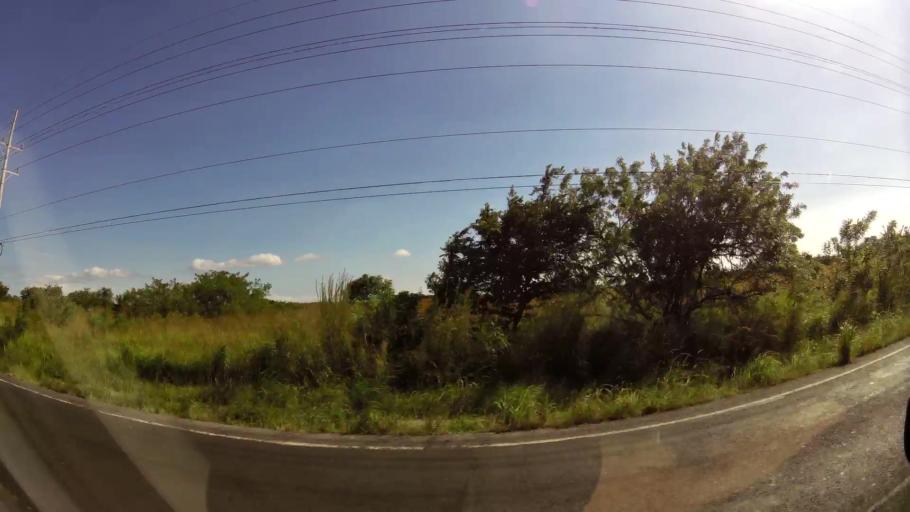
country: CR
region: Guanacaste
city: Liberia
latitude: 10.6143
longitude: -85.4812
